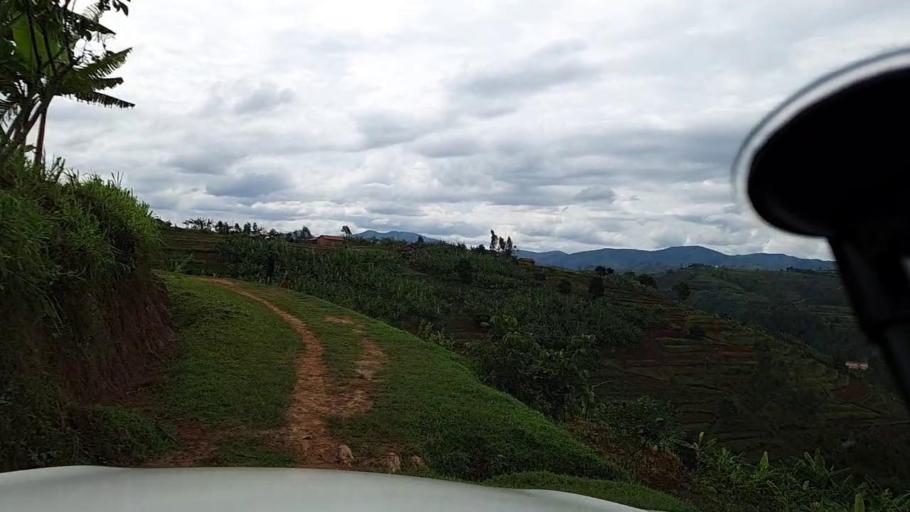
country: RW
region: Southern Province
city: Gitarama
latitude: -2.0771
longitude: 29.6426
